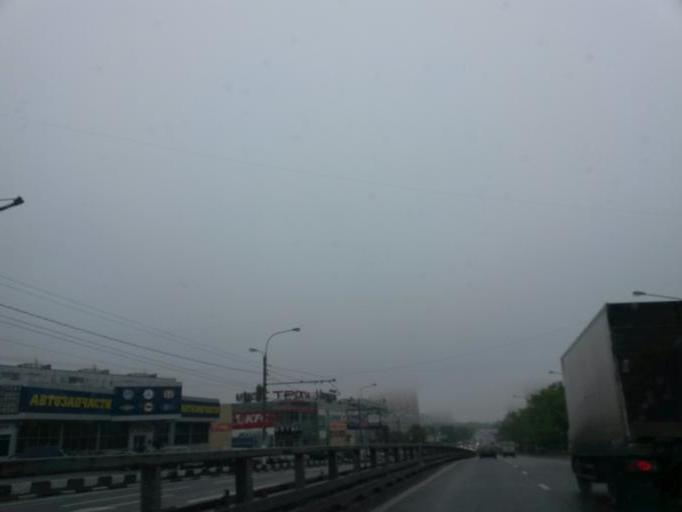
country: RU
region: Moscow
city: Yasenevo
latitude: 55.6347
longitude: 37.5209
